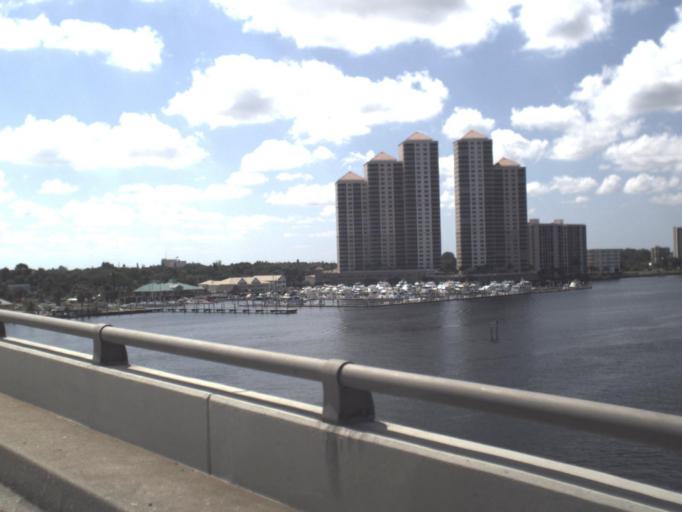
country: US
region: Florida
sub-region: Lee County
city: North Fort Myers
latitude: 26.6470
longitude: -81.8756
